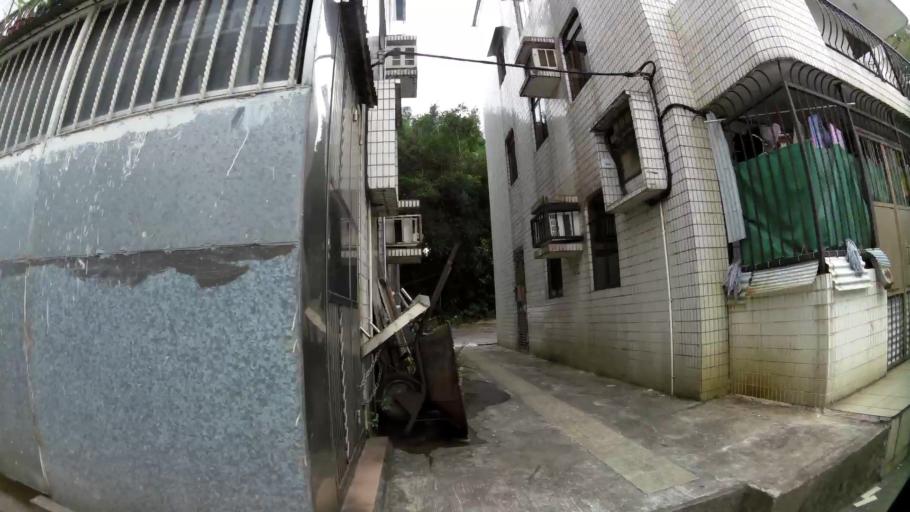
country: HK
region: Yuen Long
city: Yuen Long Kau Hui
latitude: 22.4410
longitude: 113.9907
